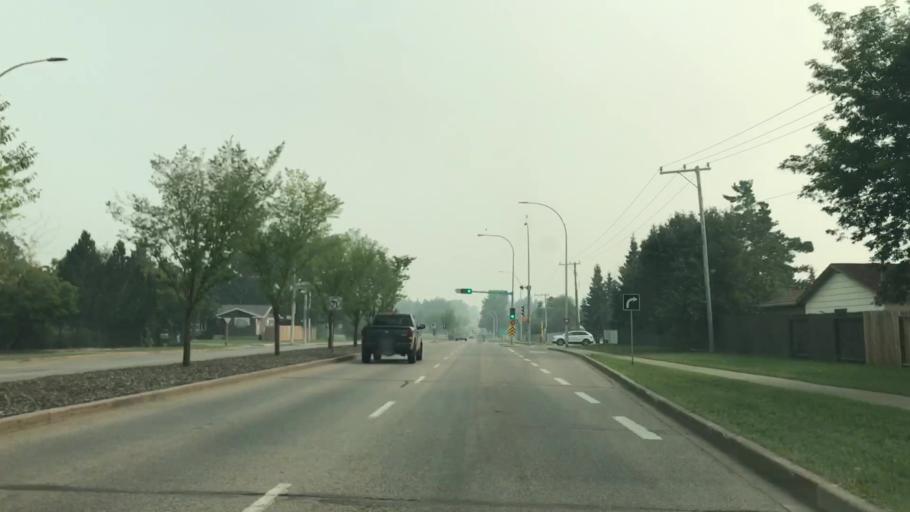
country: CA
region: Alberta
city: Sherwood Park
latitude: 53.5220
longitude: -113.3201
